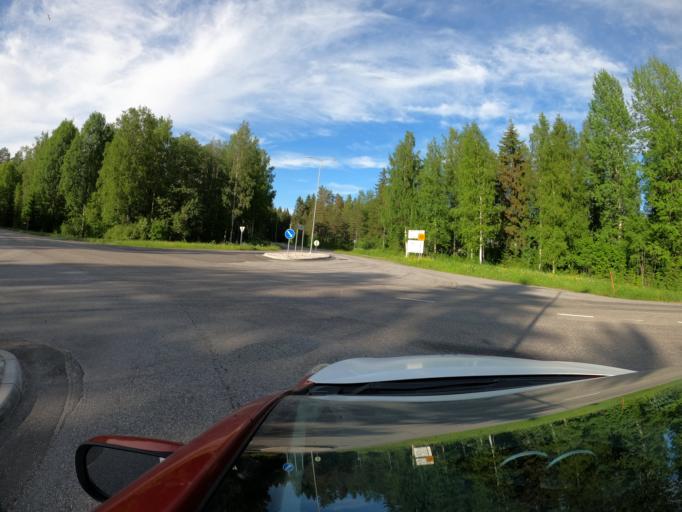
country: FI
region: Southern Savonia
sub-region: Savonlinna
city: Savonlinna
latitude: 61.8499
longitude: 28.9644
